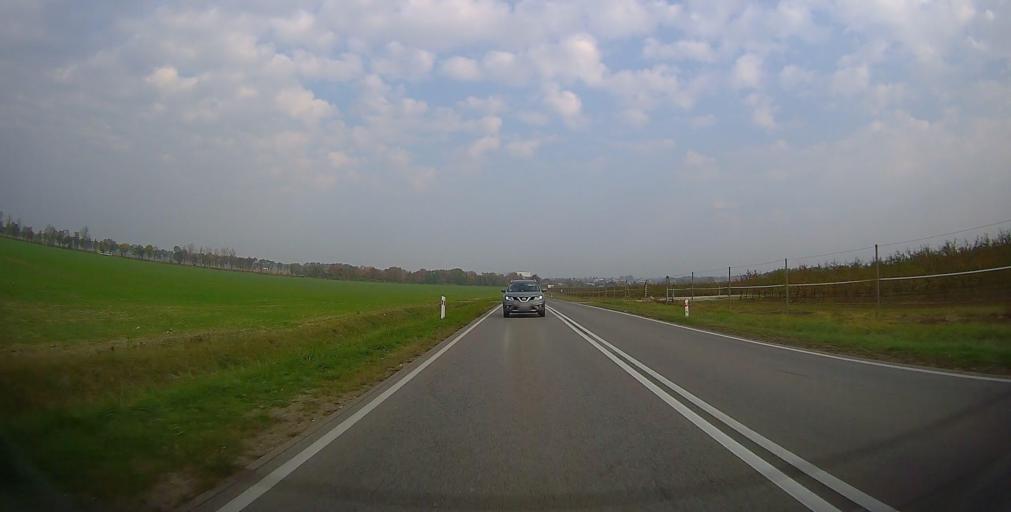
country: PL
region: Masovian Voivodeship
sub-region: Powiat grojecki
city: Belsk Duzy
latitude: 51.8031
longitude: 20.7903
